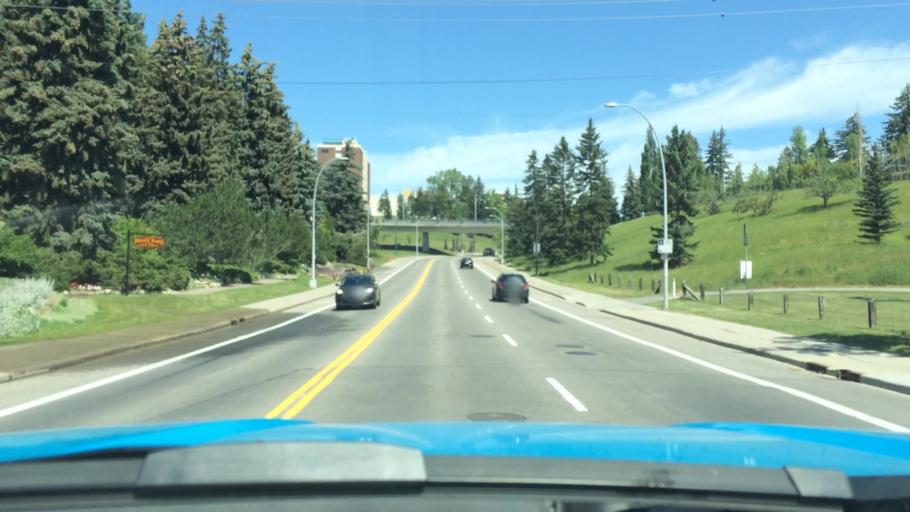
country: CA
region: Alberta
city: Calgary
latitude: 51.0594
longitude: -114.0860
